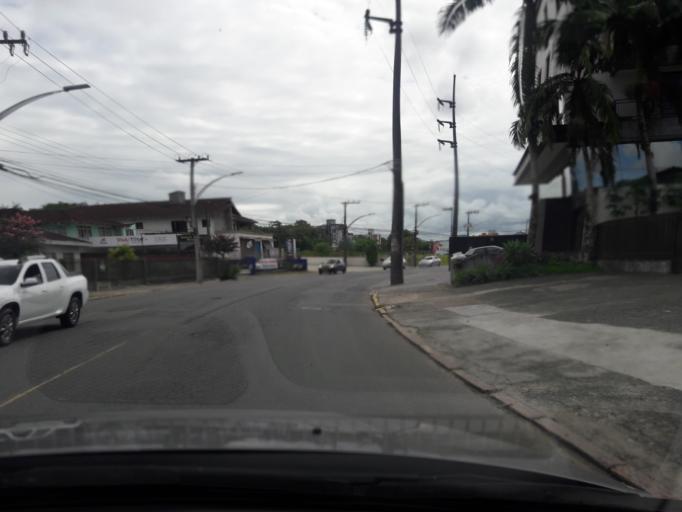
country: BR
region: Santa Catarina
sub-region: Joinville
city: Joinville
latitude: -26.3239
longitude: -48.8554
